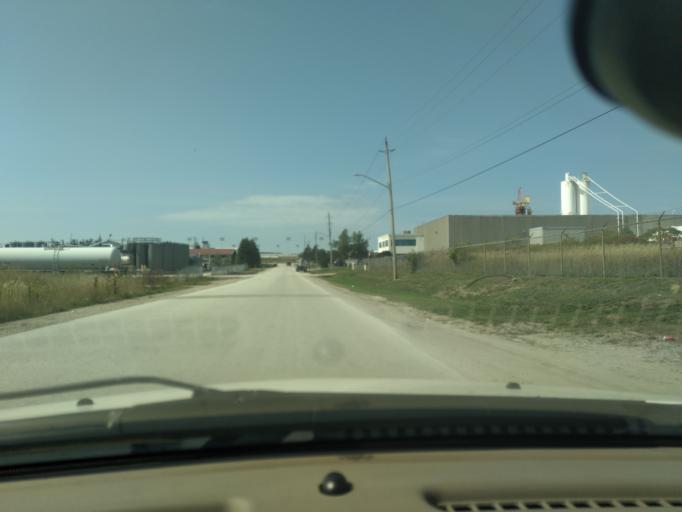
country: CA
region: Ontario
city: Innisfil
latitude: 44.2946
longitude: -79.6773
